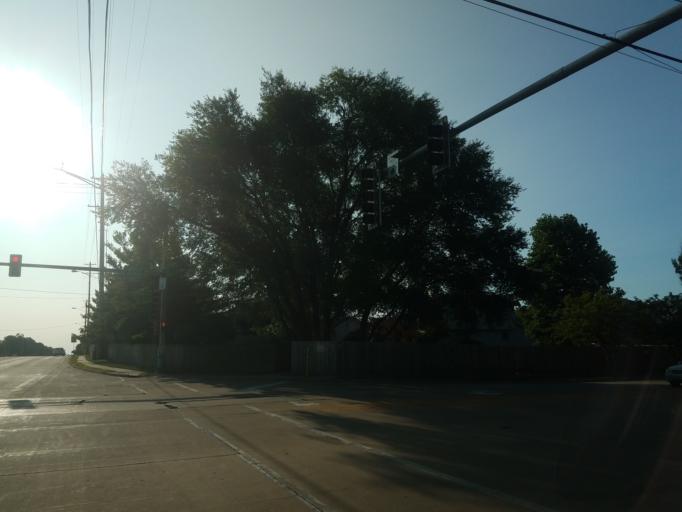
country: US
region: Illinois
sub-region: McLean County
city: Normal
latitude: 40.5316
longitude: -88.9832
